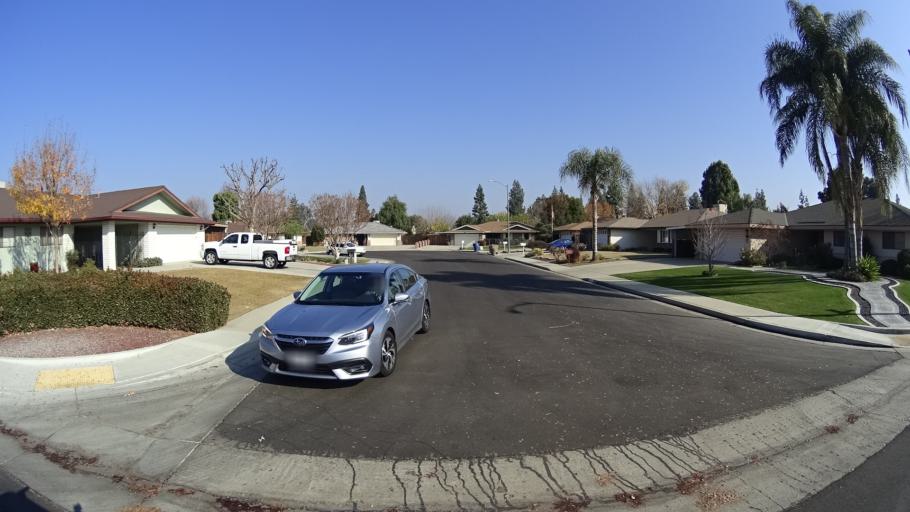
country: US
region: California
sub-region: Kern County
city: Bakersfield
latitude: 35.3499
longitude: -119.0630
